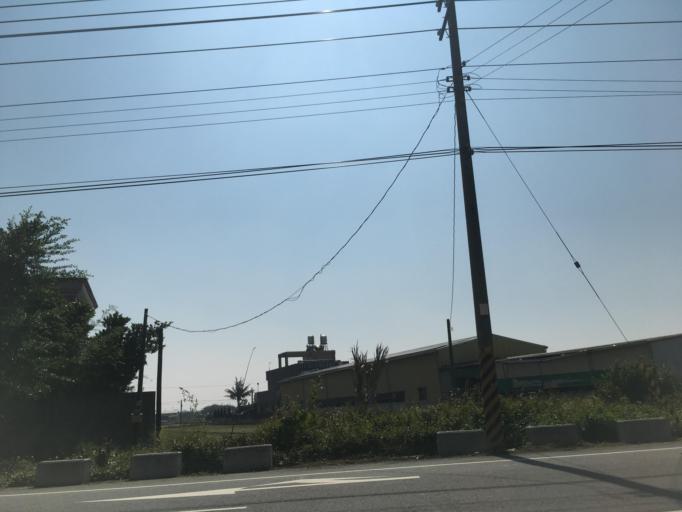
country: TW
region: Taiwan
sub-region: Chiayi
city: Jiayi Shi
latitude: 23.5603
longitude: 120.4470
